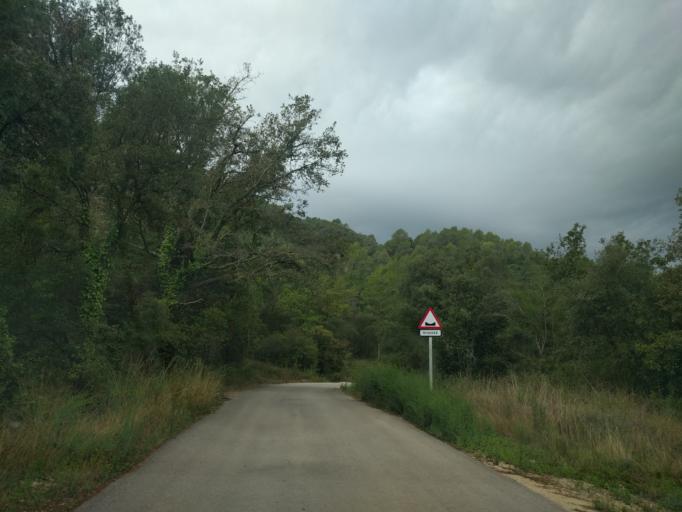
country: ES
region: Catalonia
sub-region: Provincia de Girona
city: Sant Aniol de Finestres
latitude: 42.0497
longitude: 2.6250
